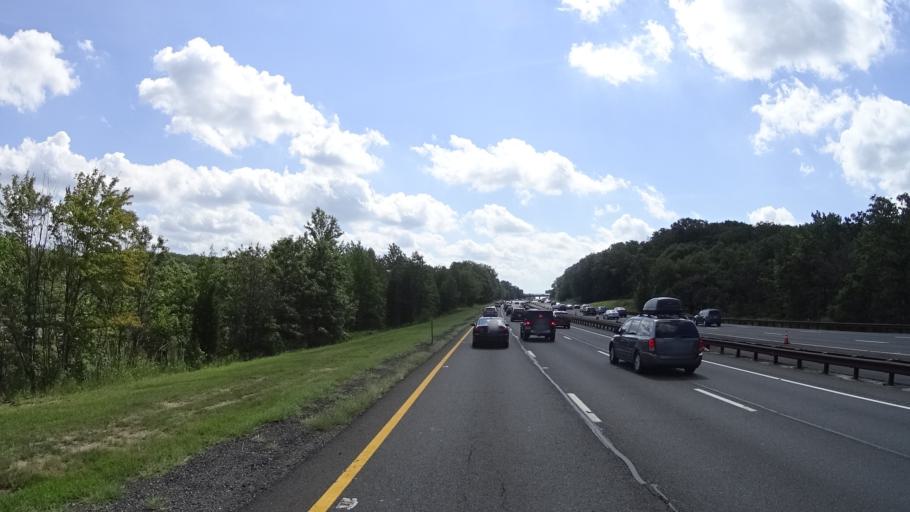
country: US
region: New Jersey
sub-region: Middlesex County
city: Laurence Harbor
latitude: 40.4387
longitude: -74.2585
